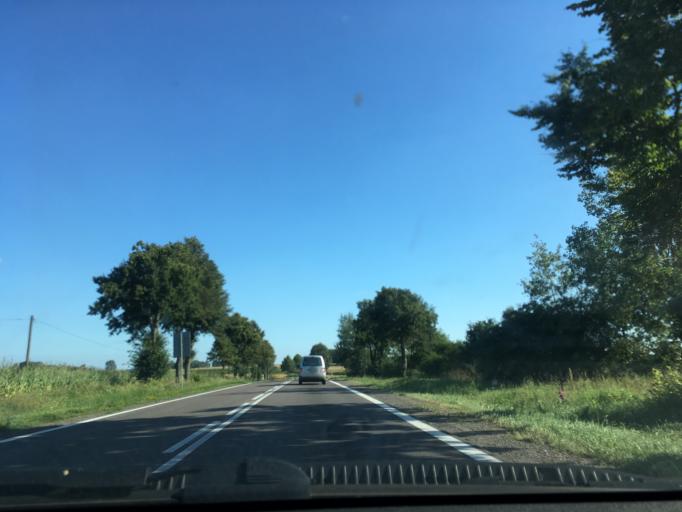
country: PL
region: Podlasie
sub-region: Powiat sokolski
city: Janow
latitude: 53.4371
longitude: 23.0978
